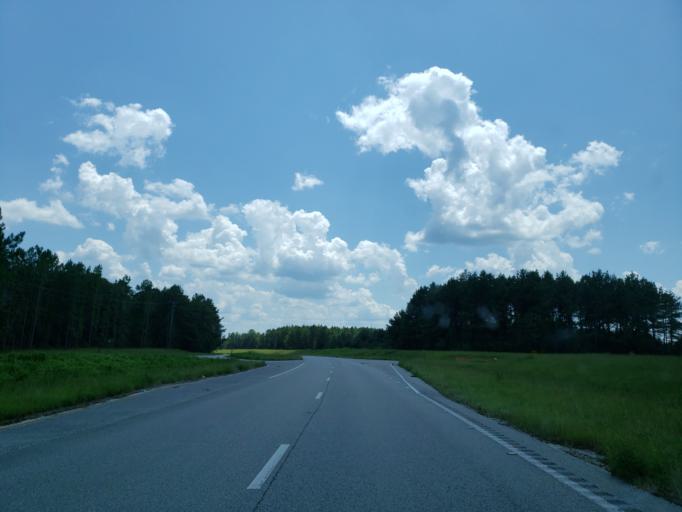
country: US
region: Mississippi
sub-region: Greene County
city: Leakesville
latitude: 31.3502
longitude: -88.5057
